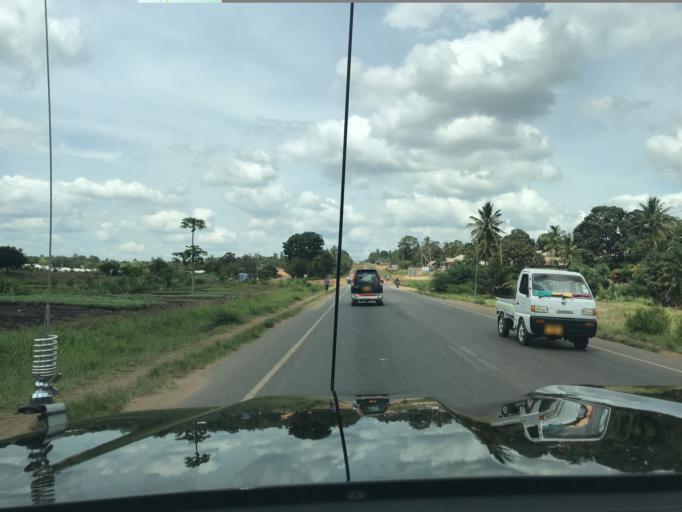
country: TZ
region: Pwani
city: Kibaha
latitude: -6.7632
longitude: 38.9493
